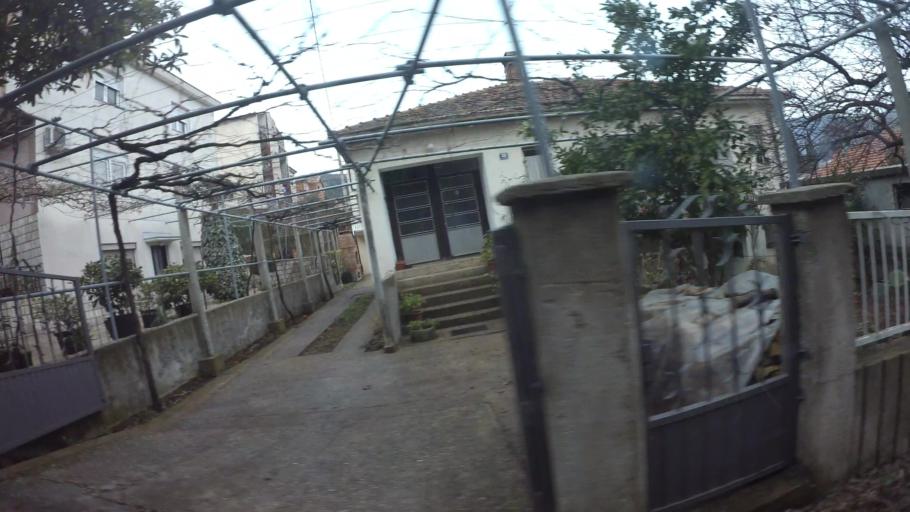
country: BA
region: Federation of Bosnia and Herzegovina
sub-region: Hercegovacko-Bosanski Kanton
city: Mostar
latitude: 43.3349
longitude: 17.8023
